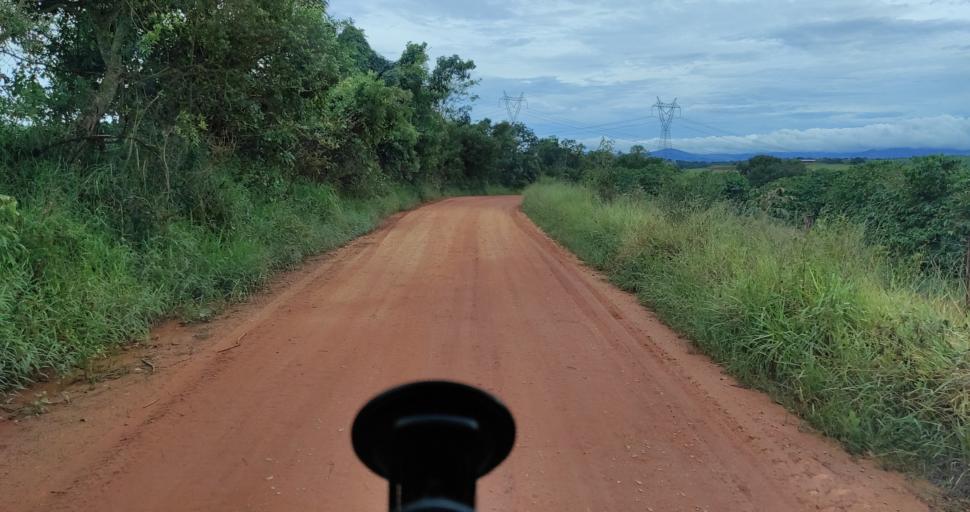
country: BR
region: Minas Gerais
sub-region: Piui
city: Piui
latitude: -20.2859
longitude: -46.3667
